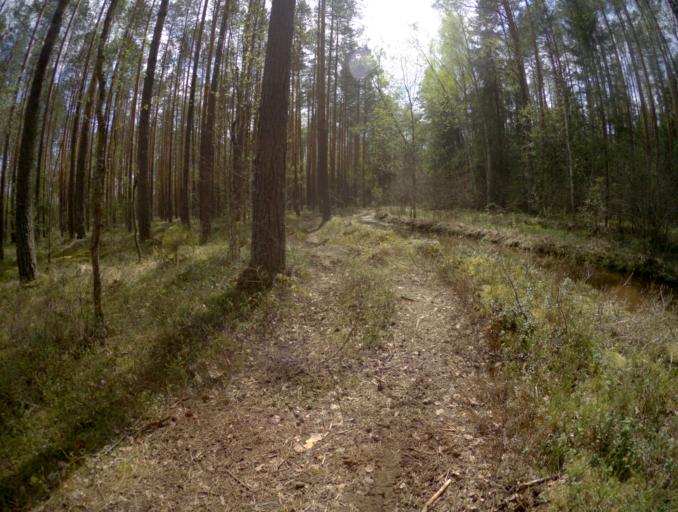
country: RU
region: Vladimir
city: Golovino
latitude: 55.9034
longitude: 40.3935
